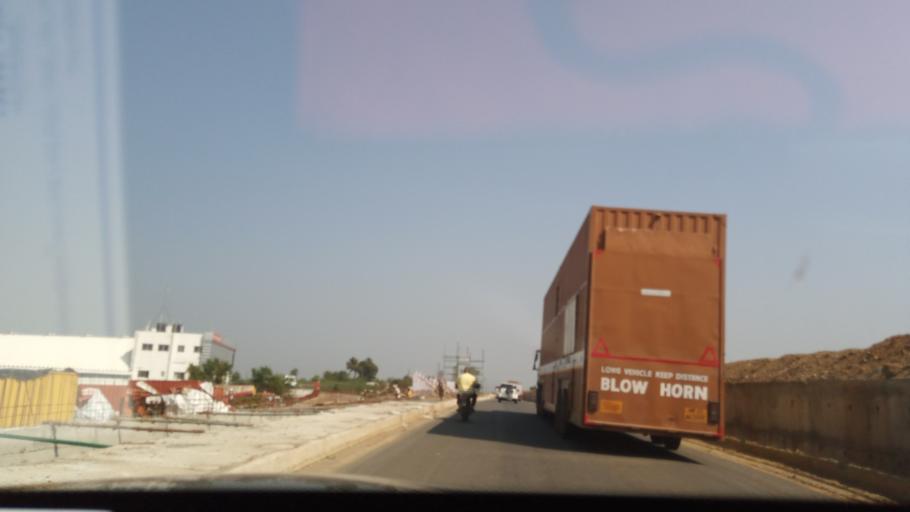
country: IN
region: Karnataka
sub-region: Dharwad
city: Hubli
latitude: 15.2494
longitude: 75.1451
